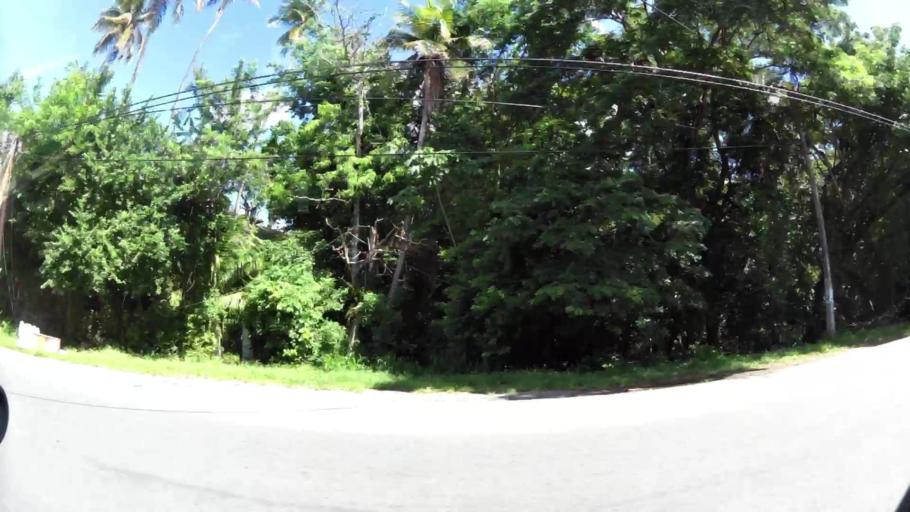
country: TT
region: Tobago
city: Scarborough
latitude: 11.1930
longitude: -60.7952
